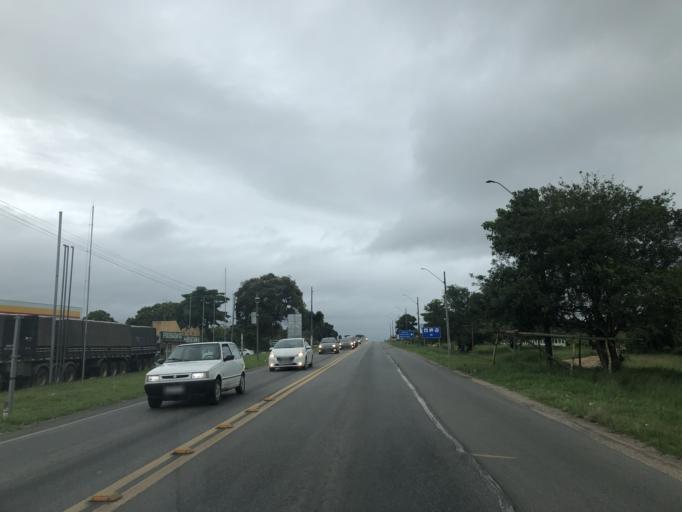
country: BR
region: Bahia
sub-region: Cruz Das Almas
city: Cruz das Almas
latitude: -12.6018
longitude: -39.0513
